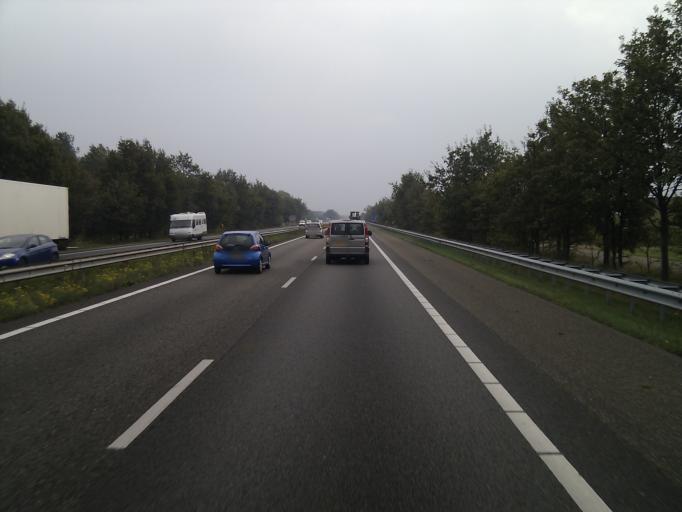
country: NL
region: North Brabant
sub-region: Gemeente Cranendonck
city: Cranendonck
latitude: 51.3318
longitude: 5.5827
